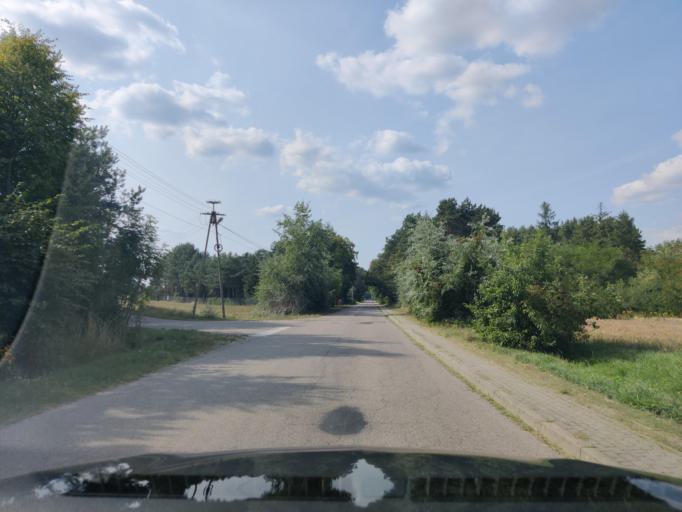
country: PL
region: Masovian Voivodeship
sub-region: Powiat wyszkowski
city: Rzasnik
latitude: 52.7724
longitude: 21.4242
